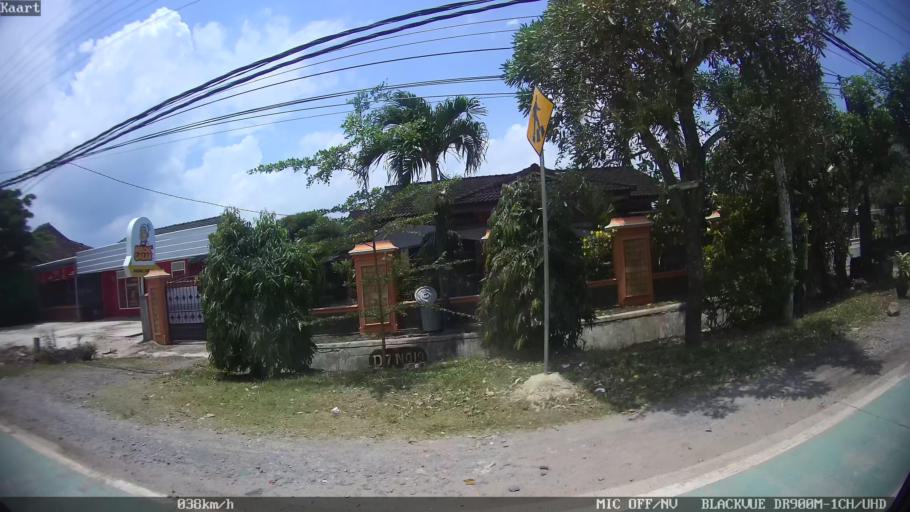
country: ID
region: Lampung
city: Kedaton
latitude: -5.3659
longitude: 105.3013
